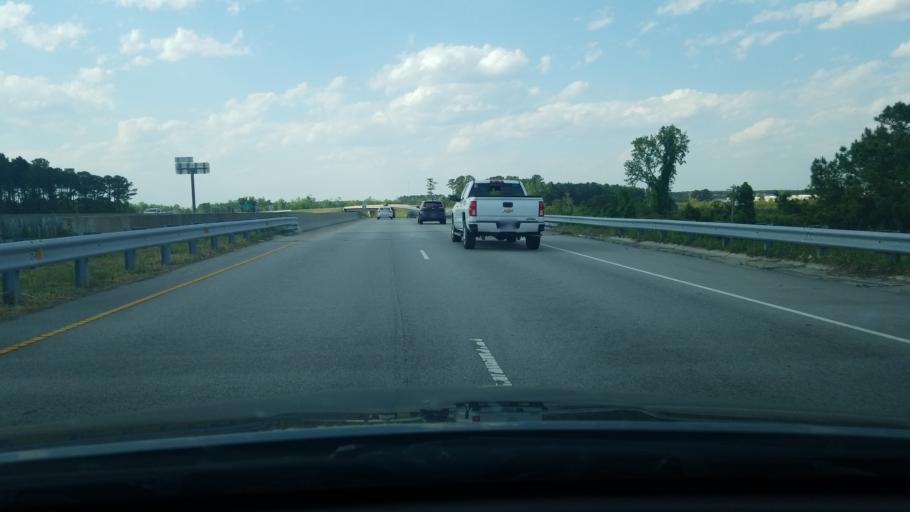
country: US
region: North Carolina
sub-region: Onslow County
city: Pumpkin Center
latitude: 34.7682
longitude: -77.3960
